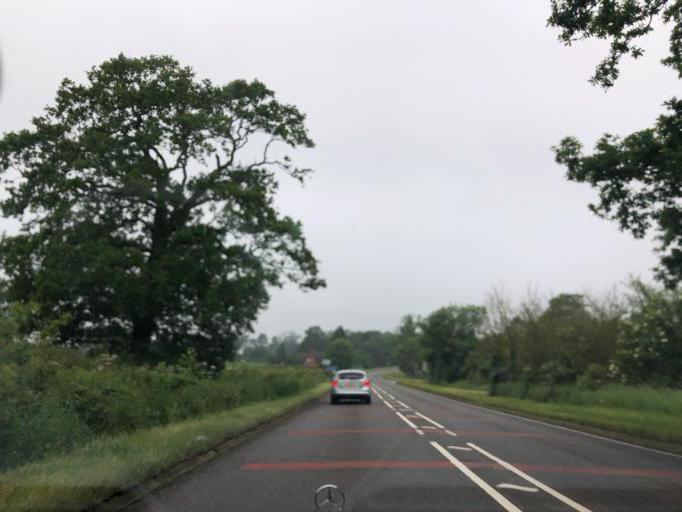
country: GB
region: England
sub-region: Warwickshire
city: Warwick
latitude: 52.2468
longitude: -1.5575
